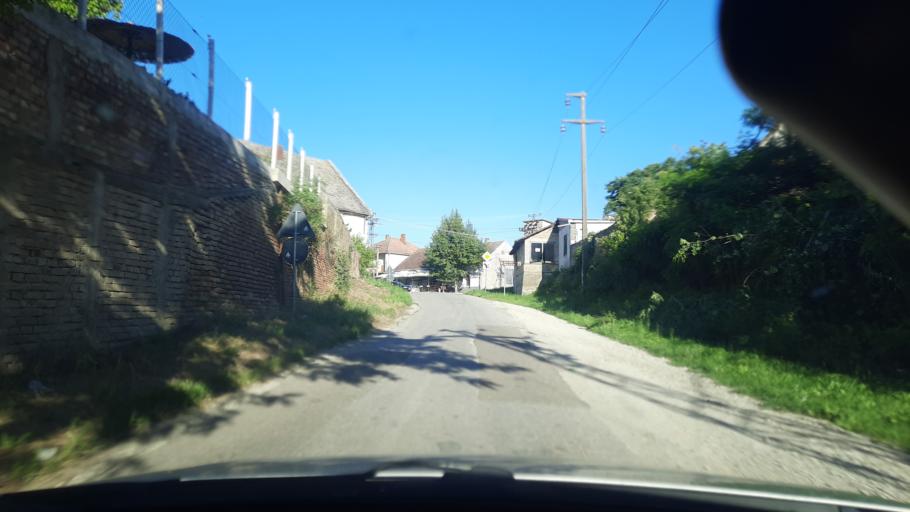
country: RS
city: Cortanovci
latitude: 45.1016
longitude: 19.9909
